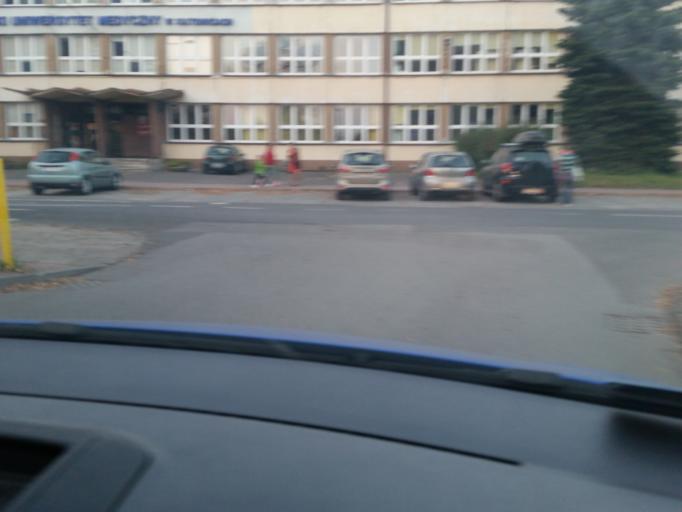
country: PL
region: Silesian Voivodeship
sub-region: Sosnowiec
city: Sosnowiec
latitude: 50.2684
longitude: 19.1314
